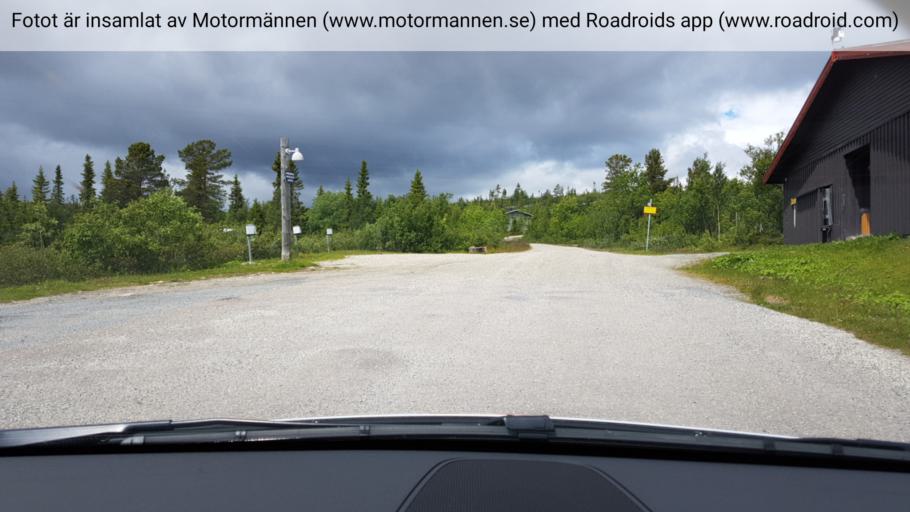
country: SE
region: Jaemtland
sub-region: Bergs Kommun
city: Hoverberg
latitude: 62.5045
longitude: 14.0972
